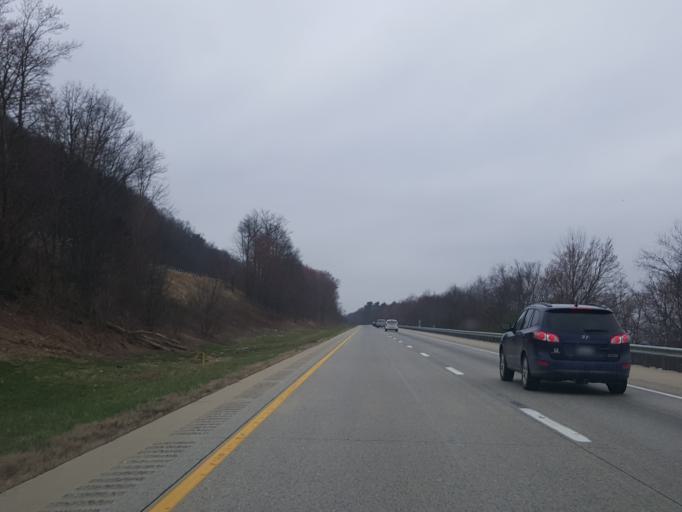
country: US
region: Pennsylvania
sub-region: Lebanon County
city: Fredericksburg
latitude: 40.5078
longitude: -76.4943
